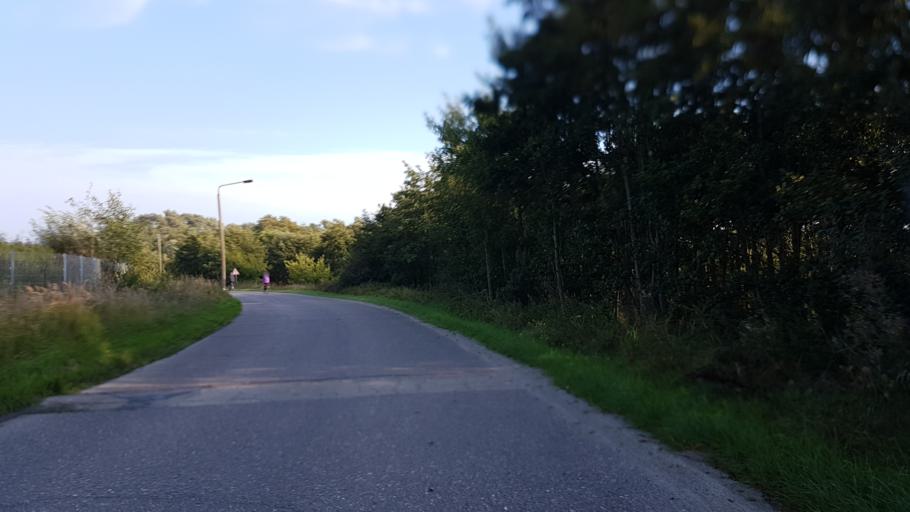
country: DE
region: Mecklenburg-Vorpommern
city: Sagard
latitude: 54.4954
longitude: 13.5529
